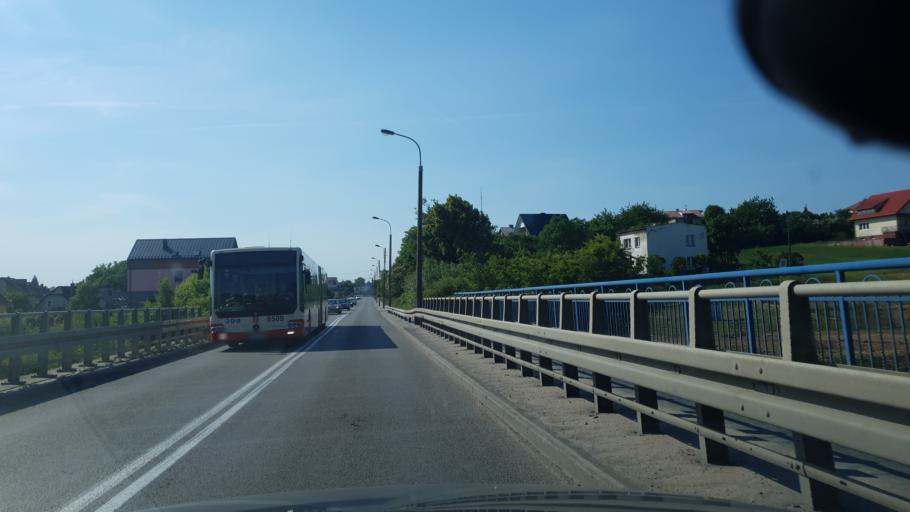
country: PL
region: Pomeranian Voivodeship
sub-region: Gdynia
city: Wielki Kack
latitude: 54.4381
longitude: 18.4621
